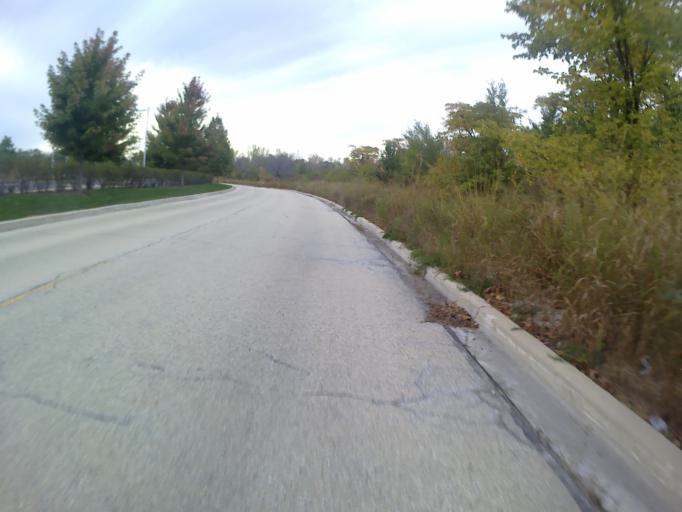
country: US
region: Illinois
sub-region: DuPage County
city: Lisle
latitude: 41.8123
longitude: -88.1039
